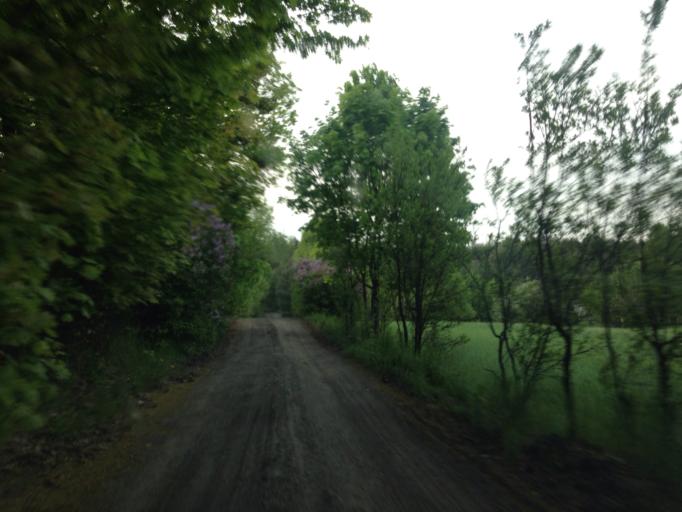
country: PL
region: Kujawsko-Pomorskie
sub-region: Powiat brodnicki
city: Brodnica
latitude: 53.3155
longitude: 19.3580
